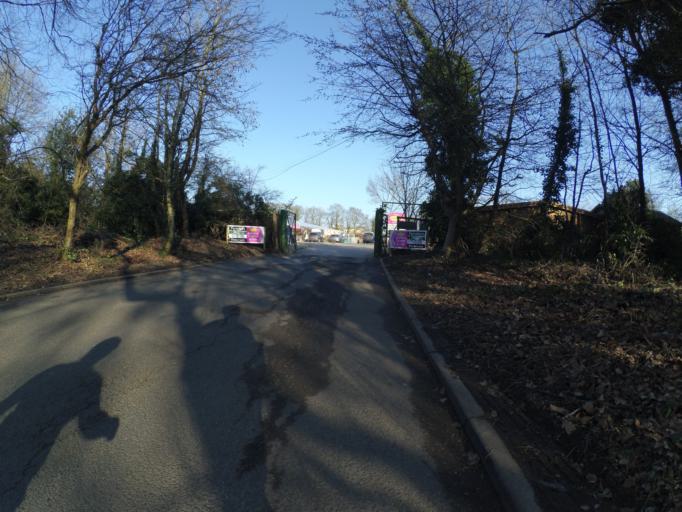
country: GB
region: England
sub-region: Greater London
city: Wembley
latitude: 51.5710
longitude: -0.2568
